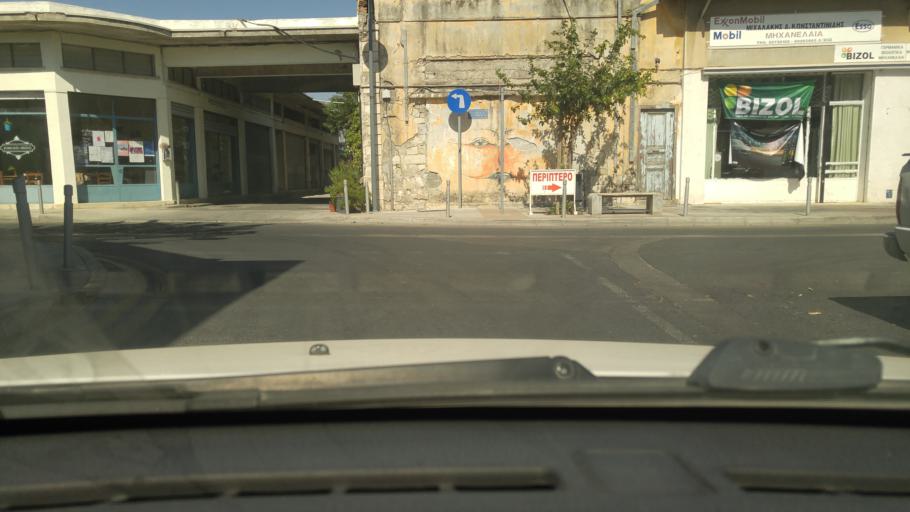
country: CY
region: Limassol
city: Limassol
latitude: 34.6744
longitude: 33.0389
